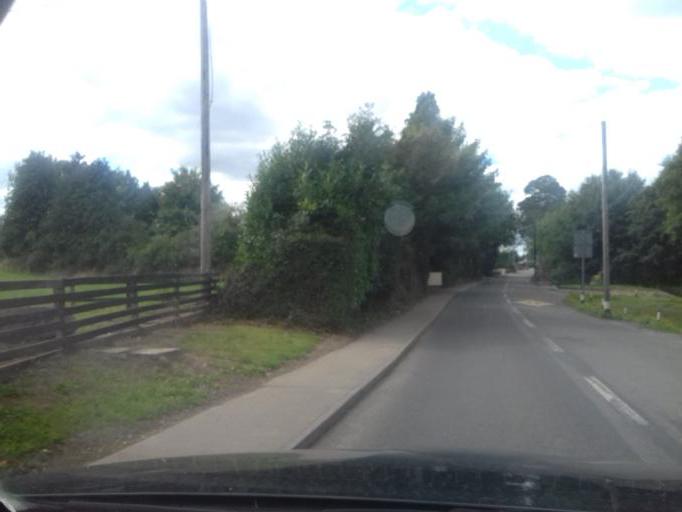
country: IE
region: Munster
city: Carrick-on-Suir
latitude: 52.2802
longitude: -7.4406
